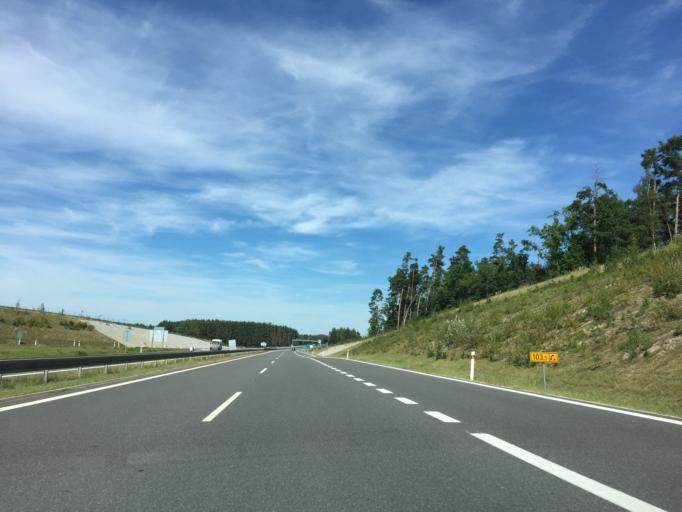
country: CZ
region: Jihocesky
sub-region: Okres Tabor
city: Veseli nad Luznici
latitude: 49.1997
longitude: 14.7014
